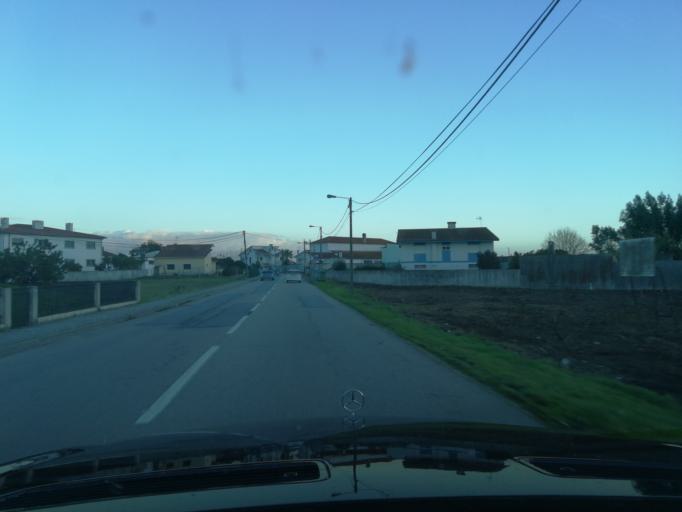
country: PT
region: Aveiro
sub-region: Estarreja
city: Estarreja
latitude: 40.7567
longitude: -8.5872
